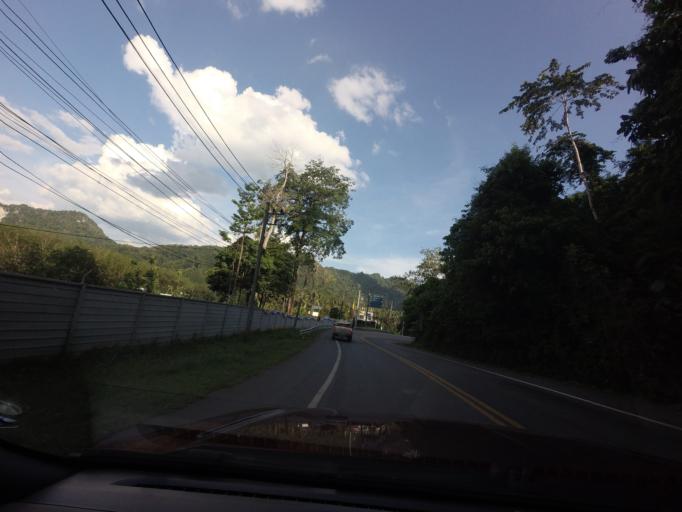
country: TH
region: Yala
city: Than To
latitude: 6.2005
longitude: 101.1742
